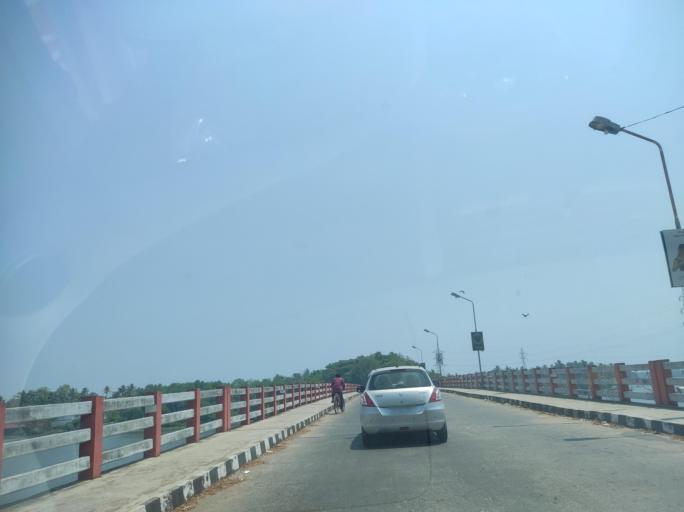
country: IN
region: Kerala
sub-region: Ernakulam
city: Cochin
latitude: 9.9018
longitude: 76.2823
